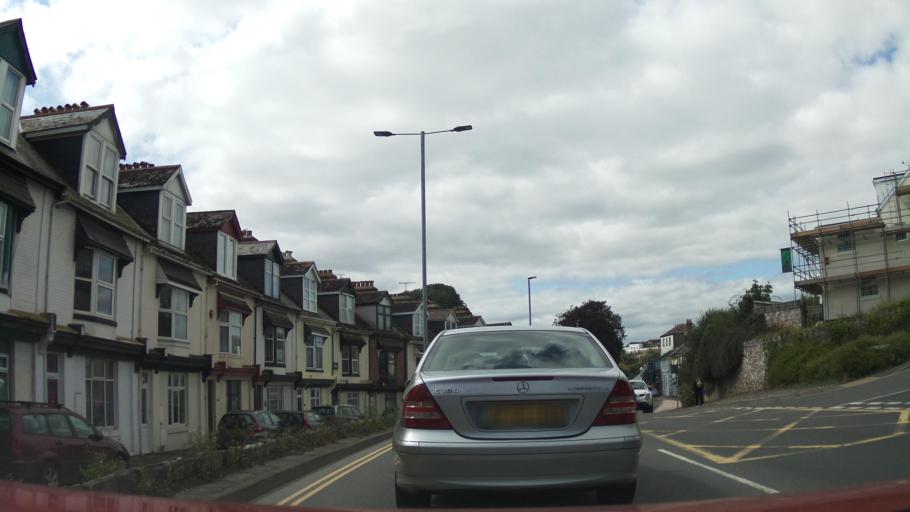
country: GB
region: England
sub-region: Devon
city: Teignmouth
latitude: 50.5476
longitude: -3.5026
